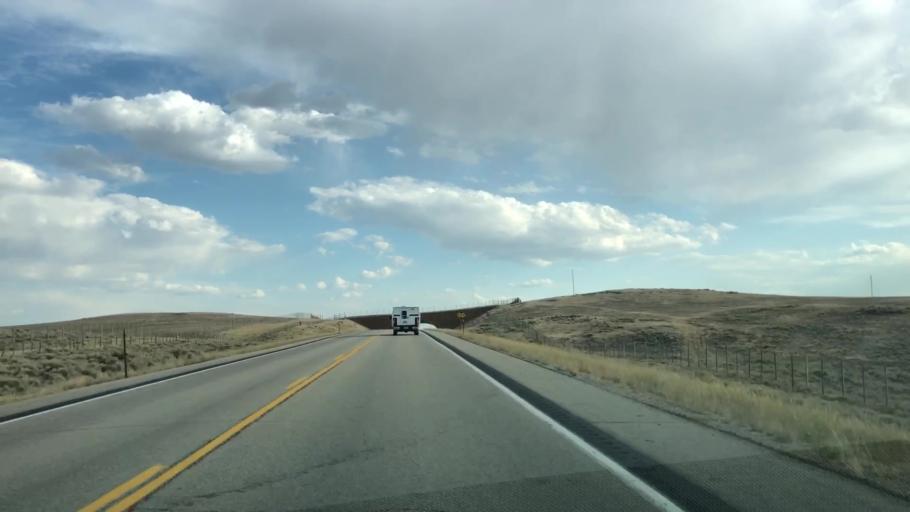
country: US
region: Wyoming
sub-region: Sublette County
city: Pinedale
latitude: 42.9165
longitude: -110.0792
